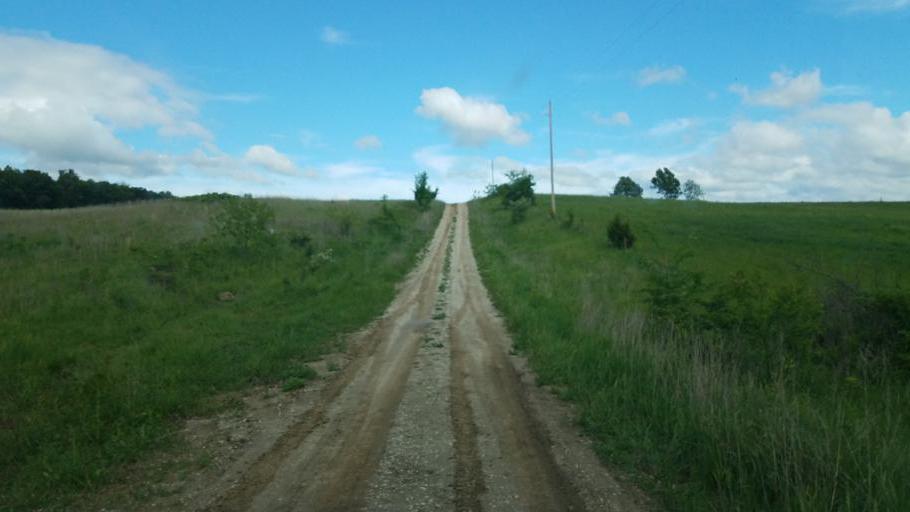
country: US
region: Missouri
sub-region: Mercer County
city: Princeton
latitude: 40.2601
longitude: -93.6956
